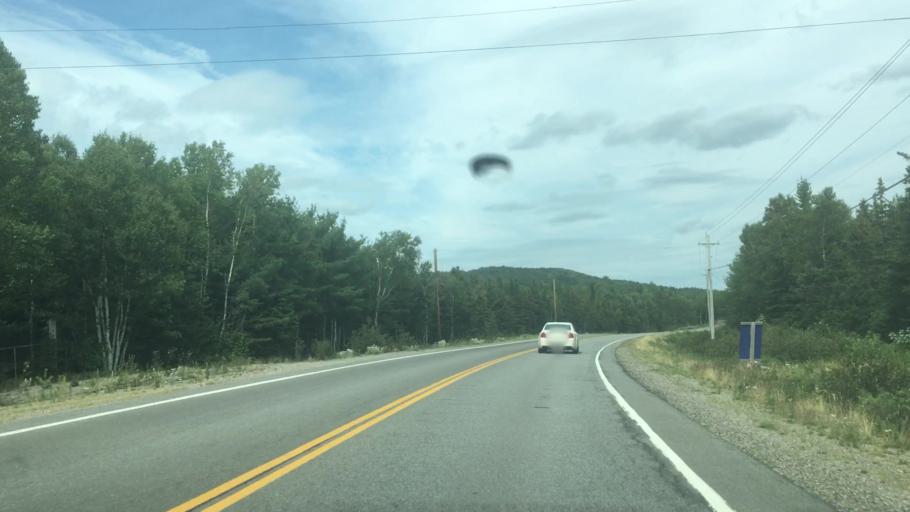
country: CA
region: Nova Scotia
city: Sydney Mines
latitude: 46.5108
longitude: -60.4310
